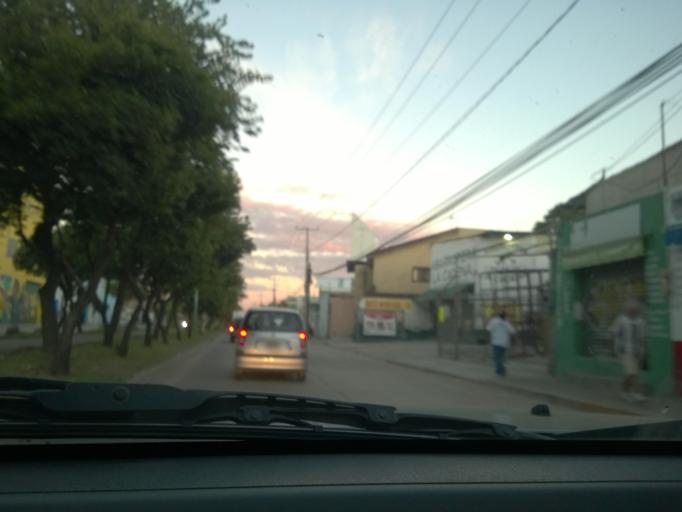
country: MX
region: Guanajuato
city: Leon
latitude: 21.1173
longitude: -101.6378
